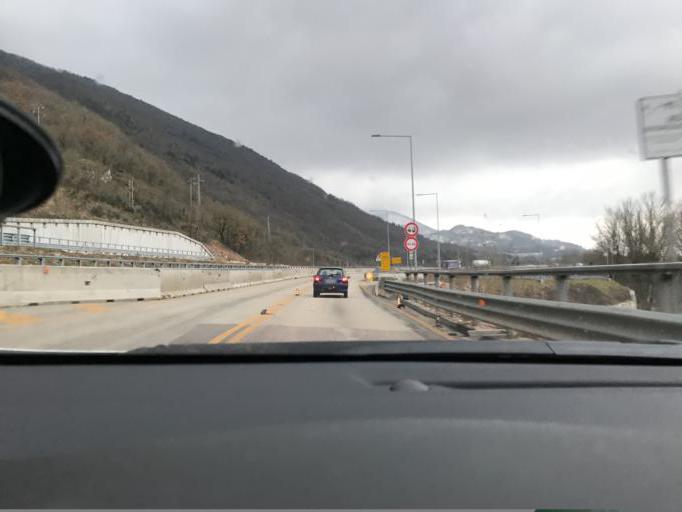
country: IT
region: The Marches
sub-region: Provincia di Ancona
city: Cerreto d'Esi
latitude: 43.3568
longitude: 12.9988
